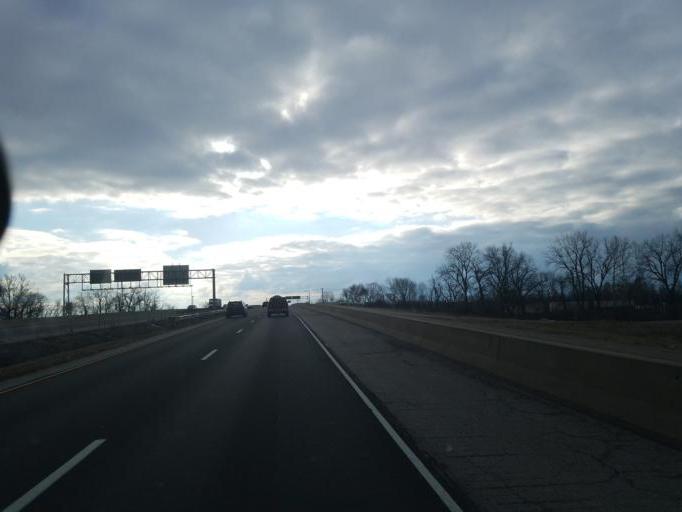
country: US
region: Illinois
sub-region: Madison County
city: Mitchell
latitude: 38.7605
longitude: -90.0973
